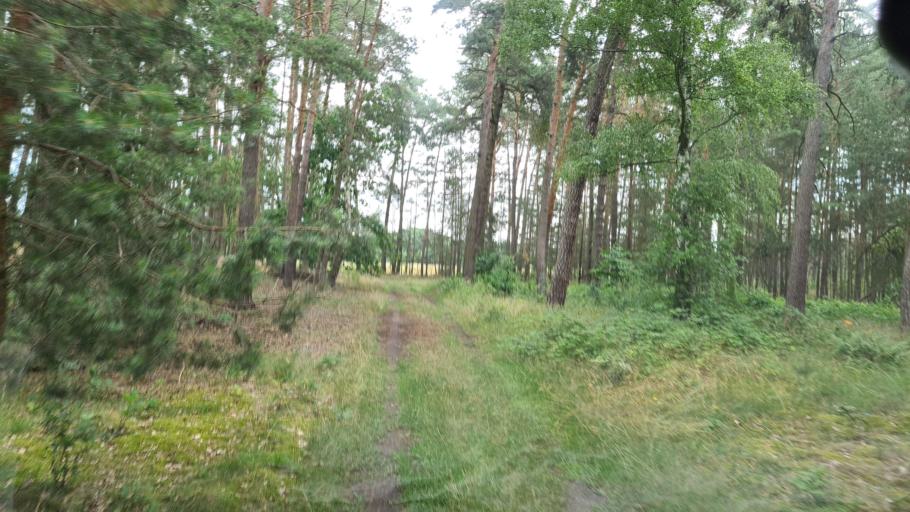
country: DE
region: Brandenburg
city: Crinitz
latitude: 51.7156
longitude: 13.8323
